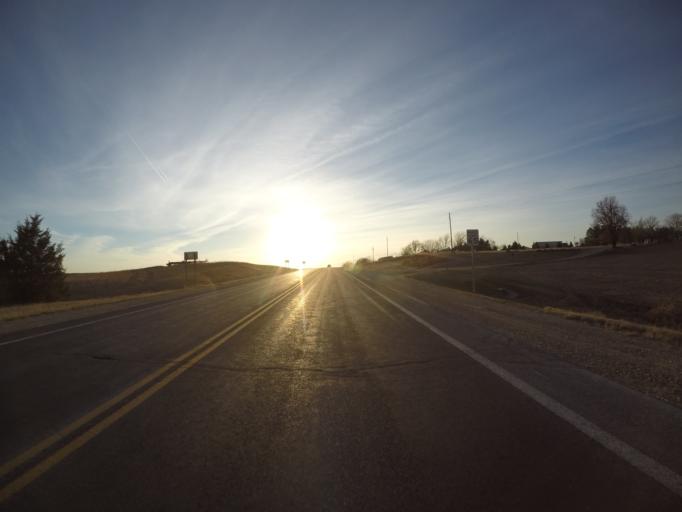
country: US
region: Kansas
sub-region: Riley County
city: Ogden
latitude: 39.2985
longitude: -96.7596
